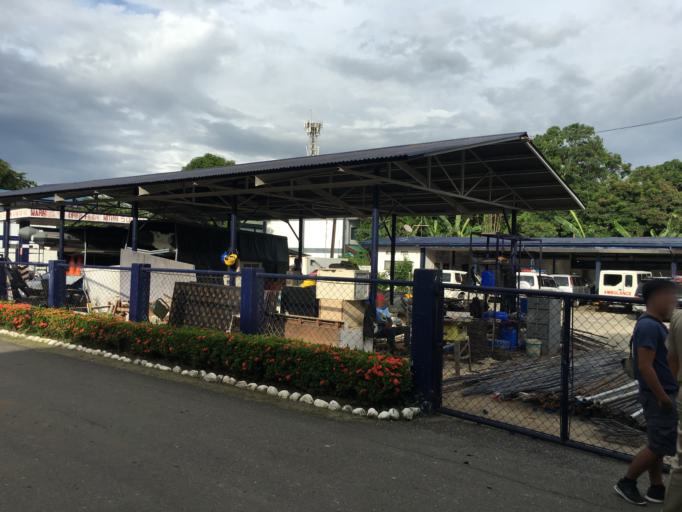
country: PH
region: Ilocos
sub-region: Province of La Union
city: San Fernando
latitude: 16.6078
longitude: 120.2905
